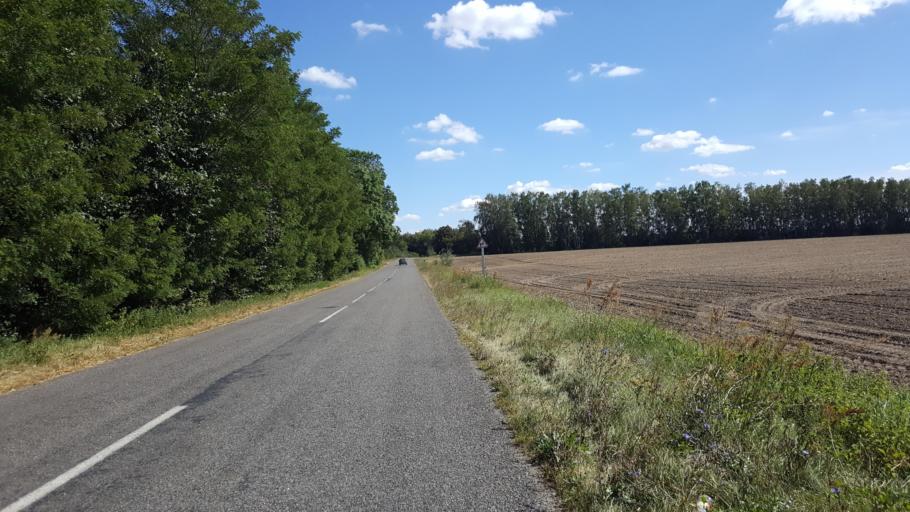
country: BY
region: Brest
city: Vysokaye
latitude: 52.2759
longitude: 23.3610
